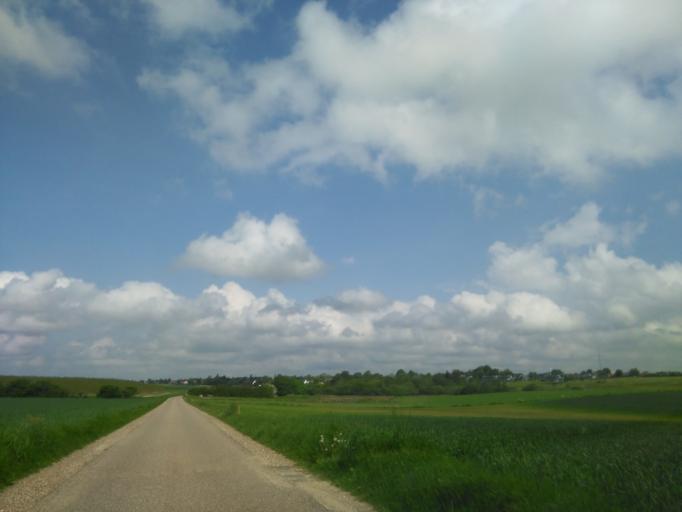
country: DK
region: Central Jutland
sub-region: Arhus Kommune
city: Sabro
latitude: 56.2123
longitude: 9.9833
